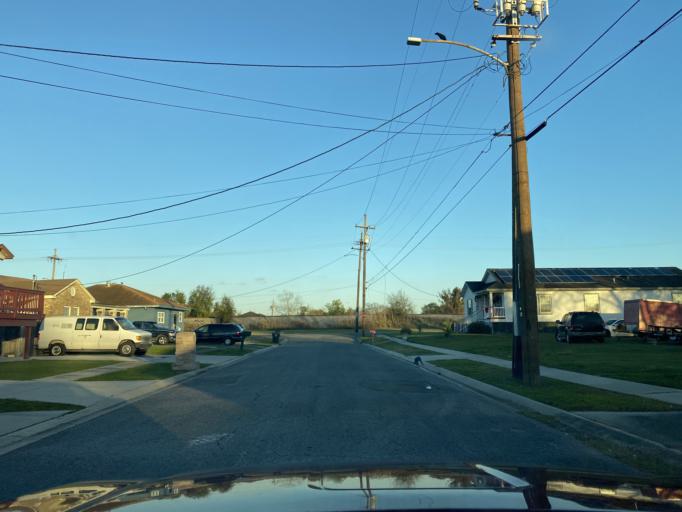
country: US
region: Louisiana
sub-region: Orleans Parish
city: New Orleans
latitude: 30.0217
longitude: -90.0481
